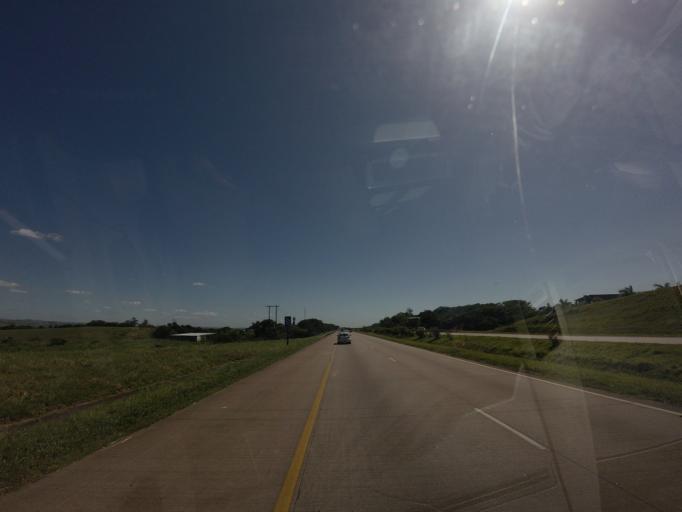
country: ZA
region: KwaZulu-Natal
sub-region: iLembe District Municipality
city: Ballitoville
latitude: -29.4881
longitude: 31.2204
